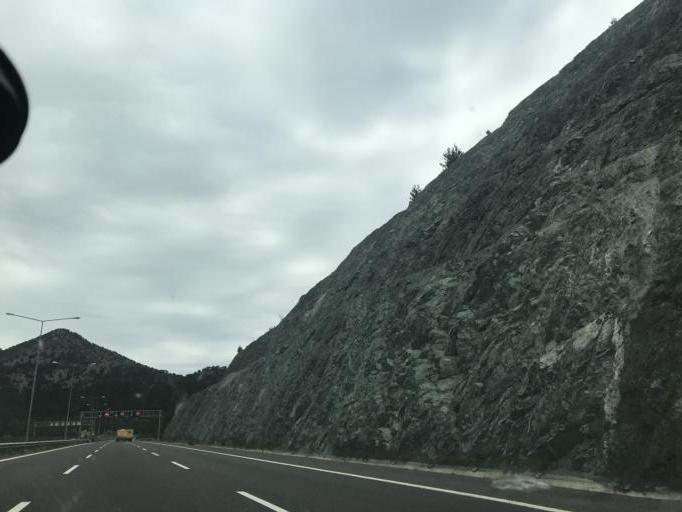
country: TR
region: Nigde
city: Ciftehan
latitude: 37.5011
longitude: 34.8253
